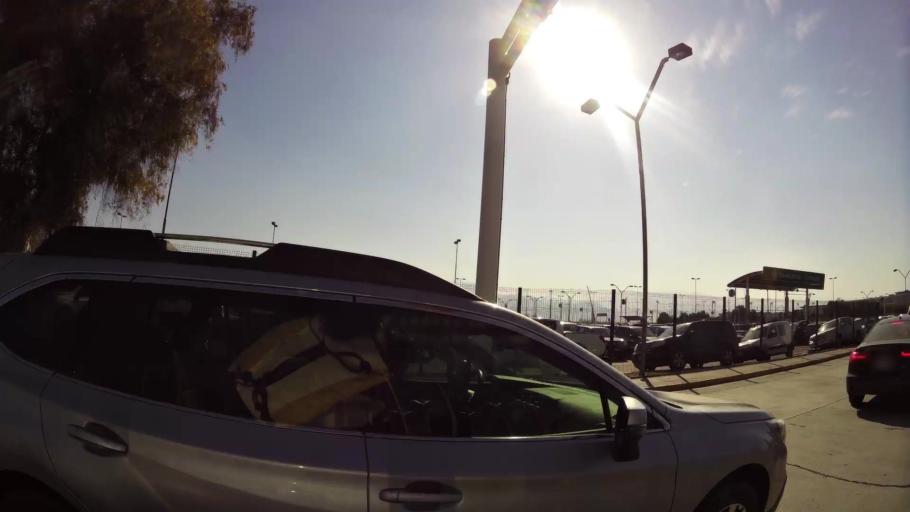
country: CL
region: Santiago Metropolitan
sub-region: Provincia de Santiago
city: Lo Prado
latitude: -33.4017
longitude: -70.7921
